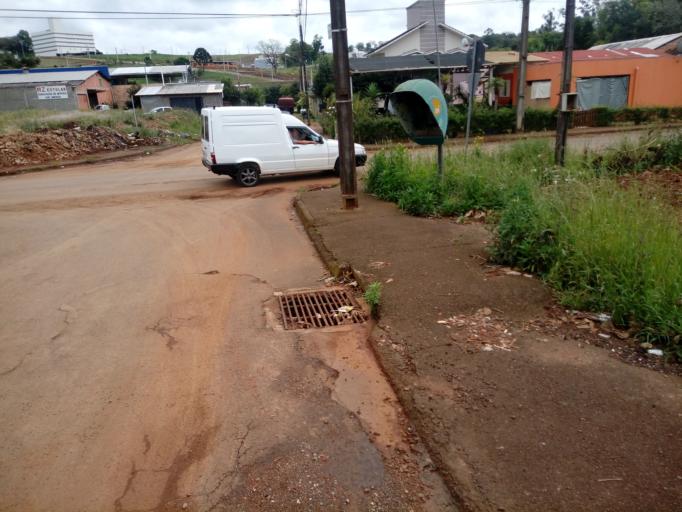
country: BR
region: Santa Catarina
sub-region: Chapeco
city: Chapeco
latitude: -27.0683
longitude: -52.6189
